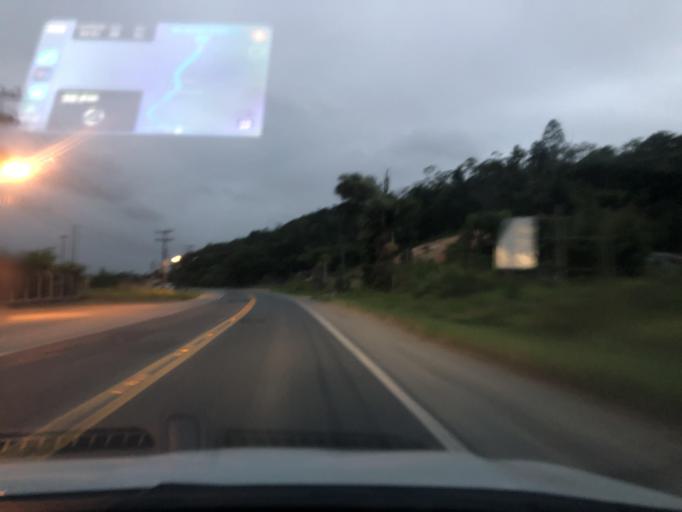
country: BR
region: Santa Catarina
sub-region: Jaragua Do Sul
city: Jaragua do Sul
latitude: -26.6405
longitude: -49.0146
